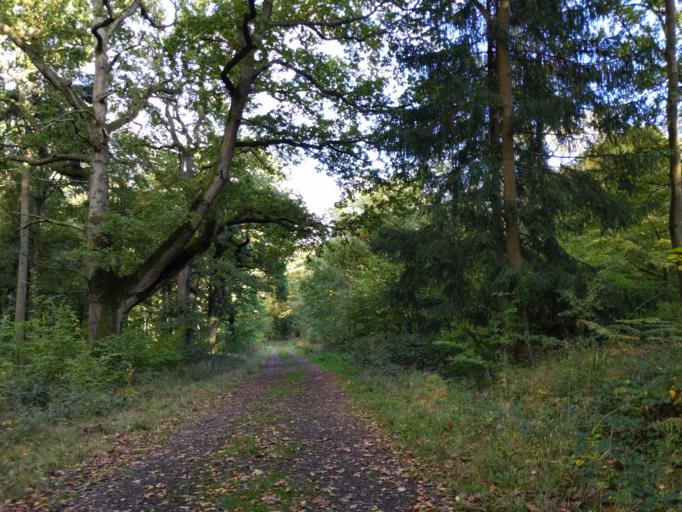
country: GB
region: England
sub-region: Oxfordshire
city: Boars Hill
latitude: 51.7203
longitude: -1.2629
